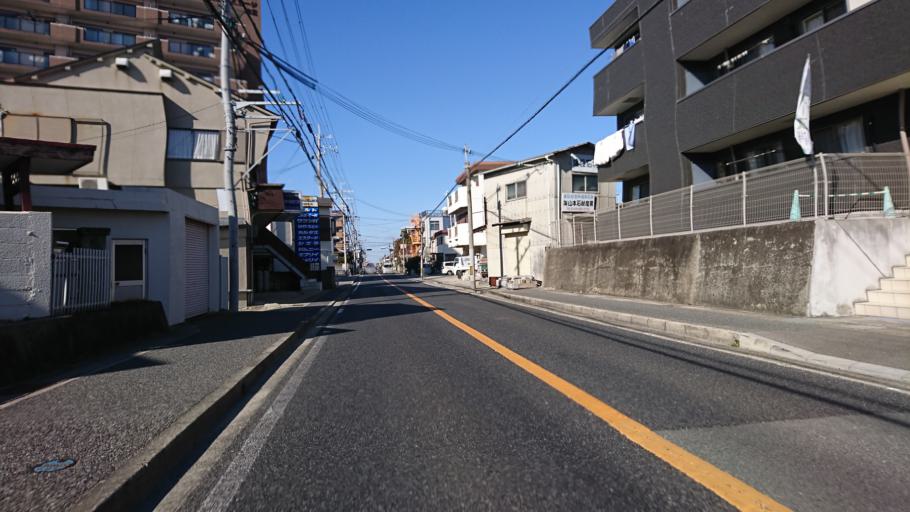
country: JP
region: Hyogo
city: Akashi
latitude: 34.6627
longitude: 134.9480
